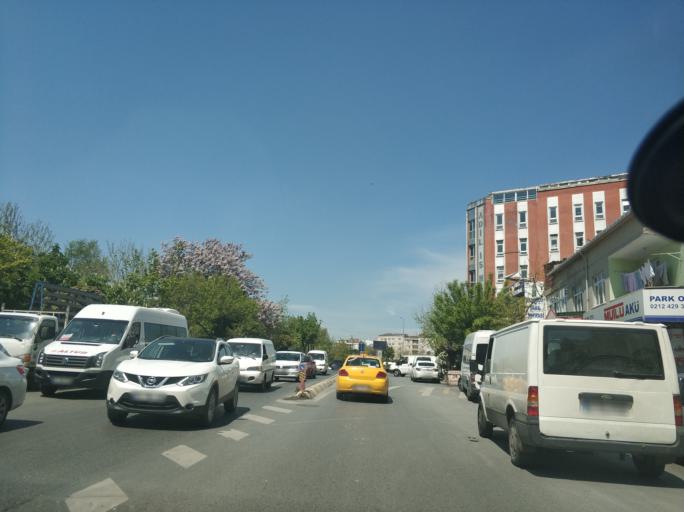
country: TR
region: Istanbul
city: Bagcilar
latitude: 41.0531
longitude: 28.8573
